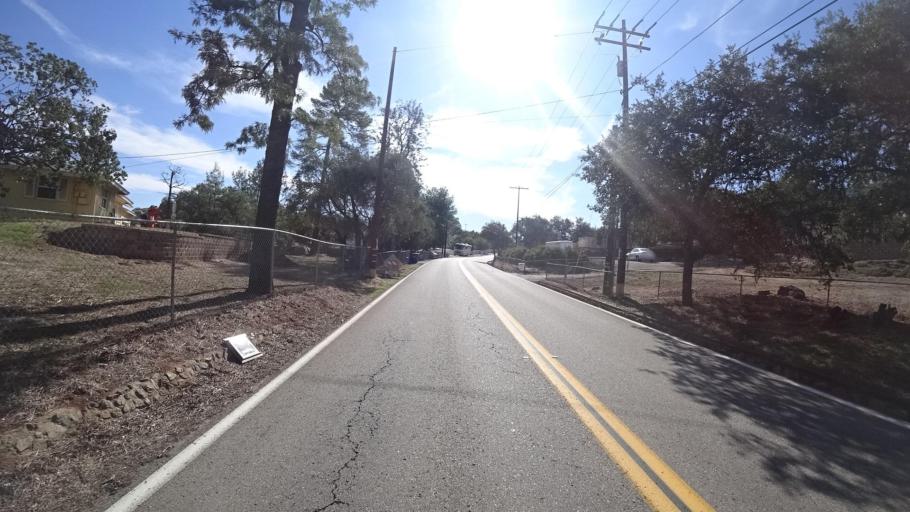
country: US
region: California
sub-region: San Diego County
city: Alpine
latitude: 32.8206
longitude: -116.7855
